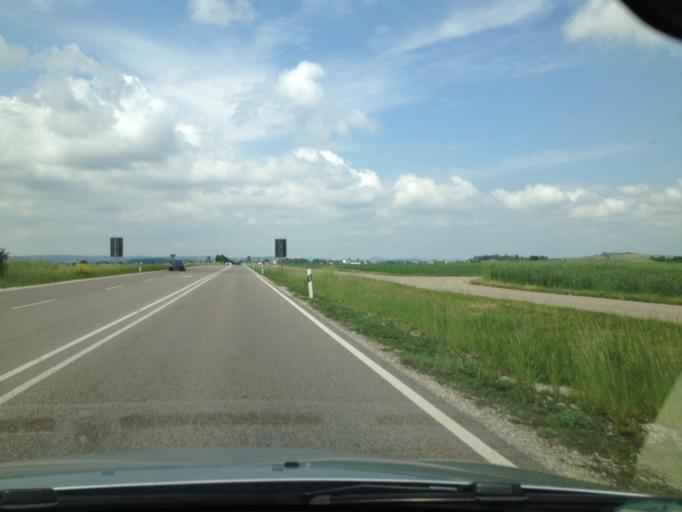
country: DE
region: Bavaria
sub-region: Swabia
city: Mottingen
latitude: 48.8002
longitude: 10.6289
